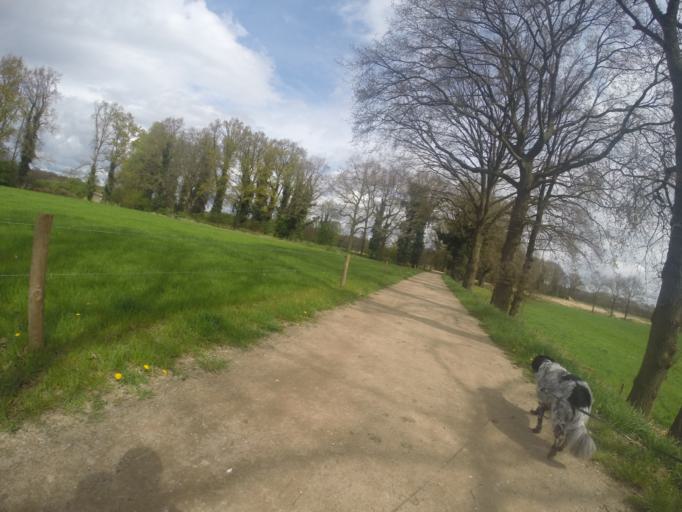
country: NL
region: Gelderland
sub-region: Gemeente Bronckhorst
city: Baak
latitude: 52.0941
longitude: 6.2689
